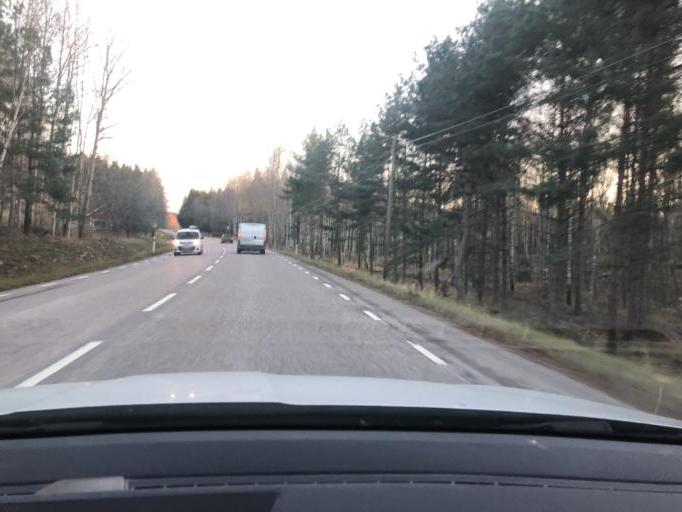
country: SE
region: Soedermanland
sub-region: Strangnas Kommun
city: Akers Styckebruk
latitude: 59.2964
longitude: 17.1021
